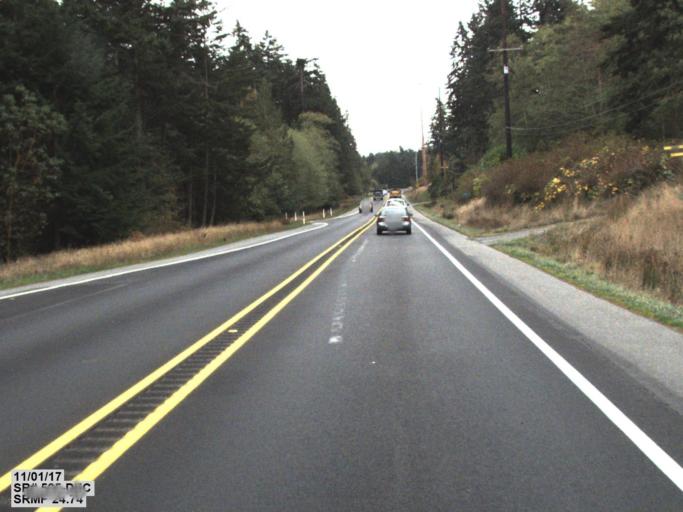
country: US
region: Washington
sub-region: Island County
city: Camano
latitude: 48.0934
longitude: -122.5706
